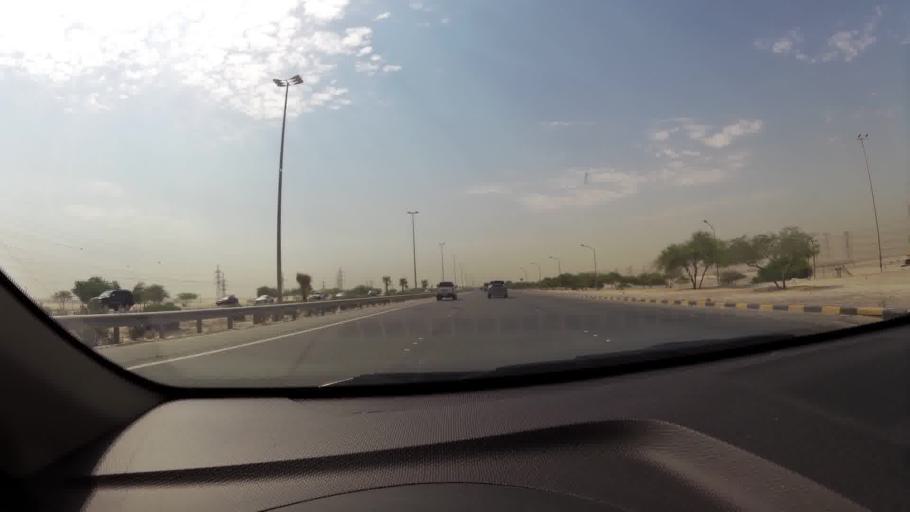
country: KW
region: Al Ahmadi
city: Al Fahahil
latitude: 28.8782
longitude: 48.2302
